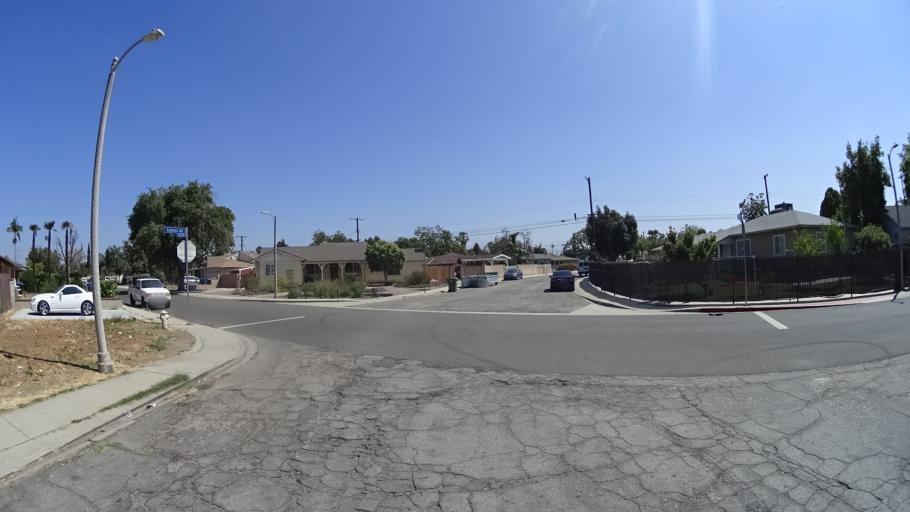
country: US
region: California
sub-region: Los Angeles County
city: Van Nuys
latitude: 34.2259
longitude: -118.4459
